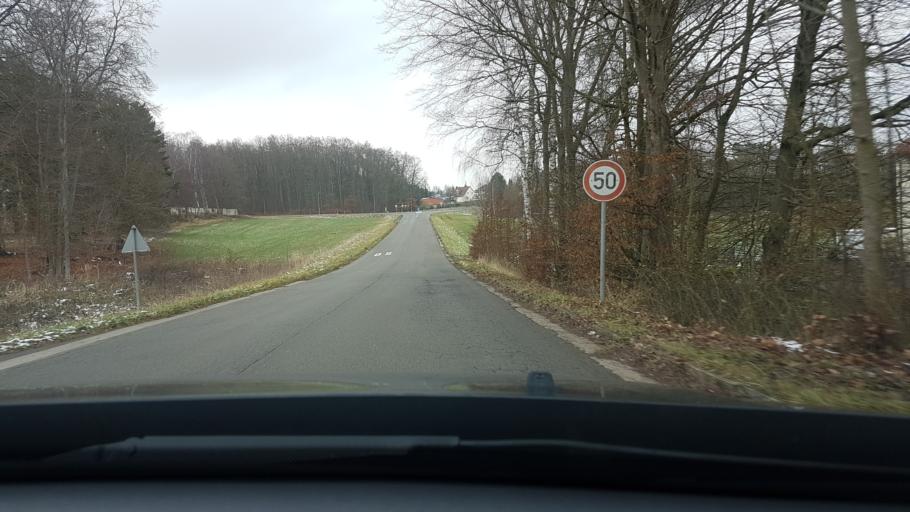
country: DE
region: Hesse
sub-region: Regierungsbezirk Kassel
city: Wolfhagen
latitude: 51.3377
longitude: 9.1272
